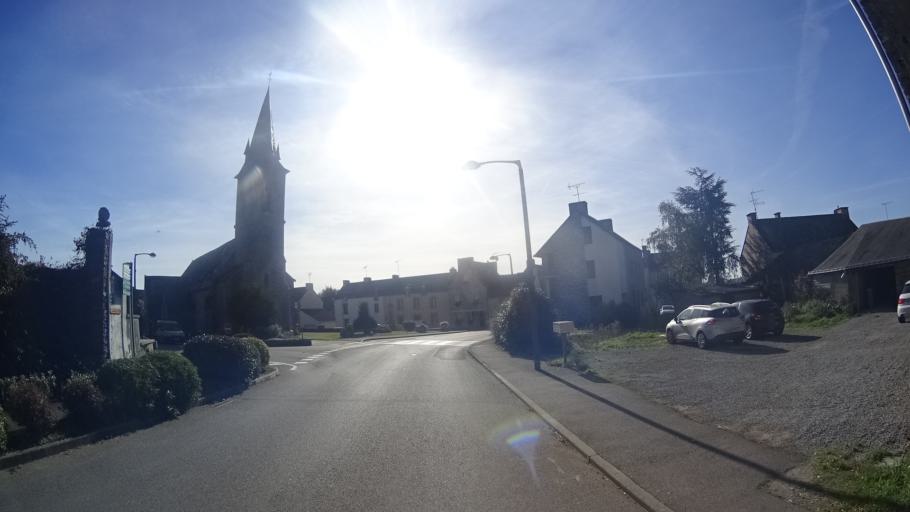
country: FR
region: Brittany
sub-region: Departement du Morbihan
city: Peillac
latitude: 47.7405
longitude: -2.2133
